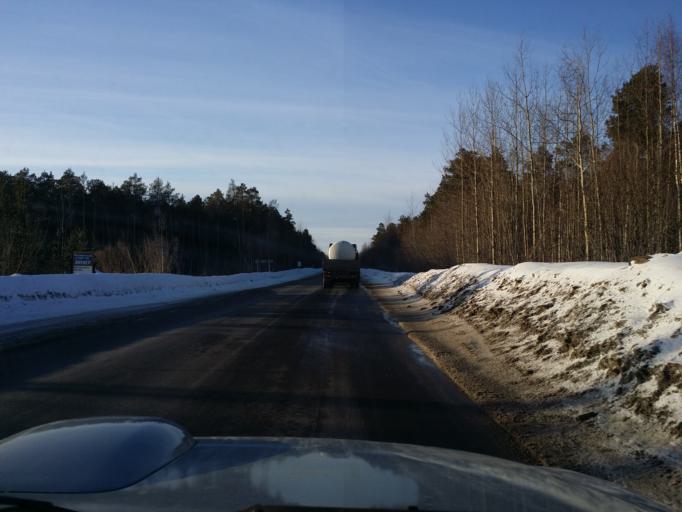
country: RU
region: Khanty-Mansiyskiy Avtonomnyy Okrug
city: Izluchinsk
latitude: 60.9441
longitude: 76.8560
